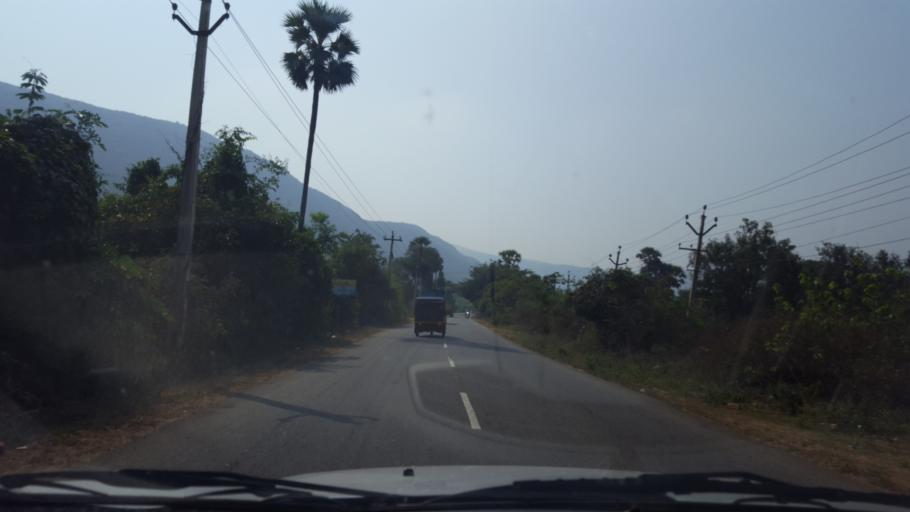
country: IN
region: Andhra Pradesh
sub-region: Vishakhapatnam
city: Vepagunta
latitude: 17.8034
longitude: 83.2561
